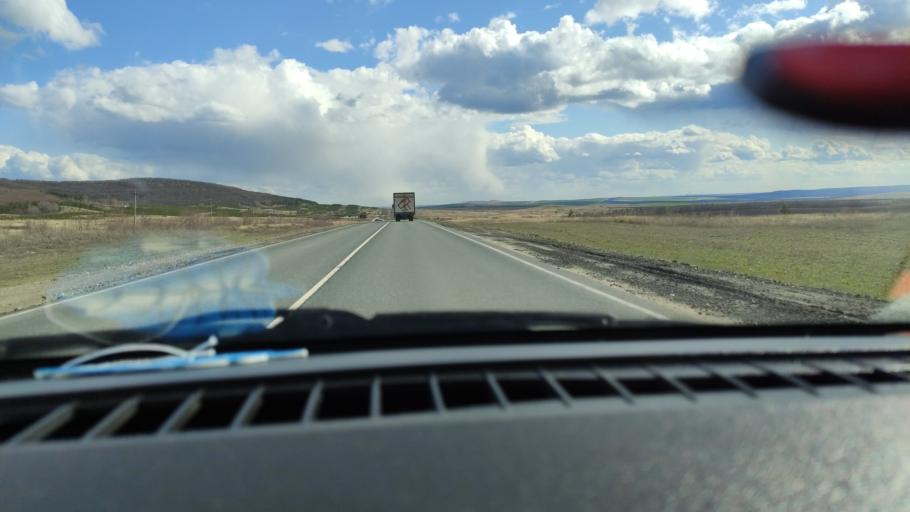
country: RU
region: Saratov
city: Alekseyevka
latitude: 52.3163
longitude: 47.9229
